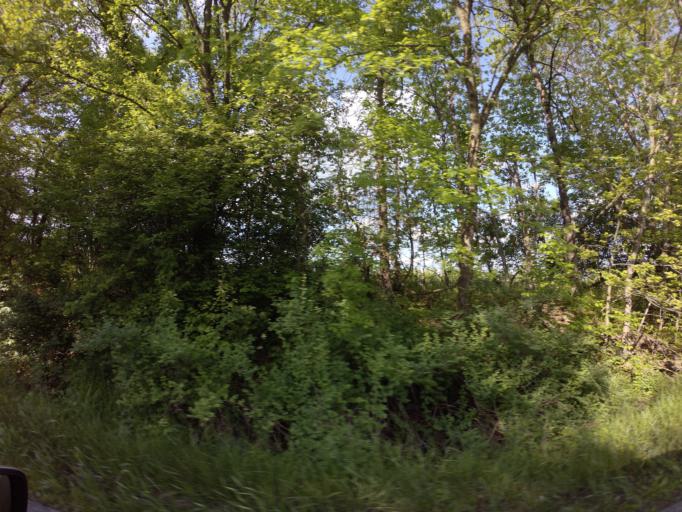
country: US
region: Maryland
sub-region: Baltimore County
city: Hunt Valley
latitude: 39.4994
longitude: -76.6884
